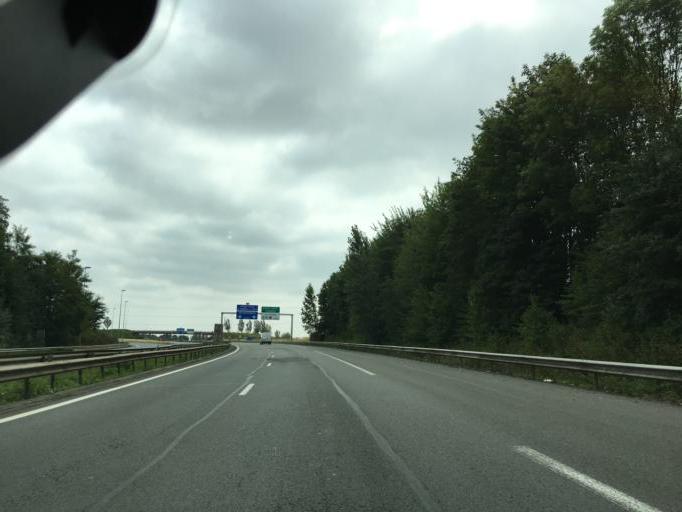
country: FR
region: Nord-Pas-de-Calais
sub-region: Departement du Pas-de-Calais
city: Courcelles-les-Lens
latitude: 50.4127
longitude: 3.0328
